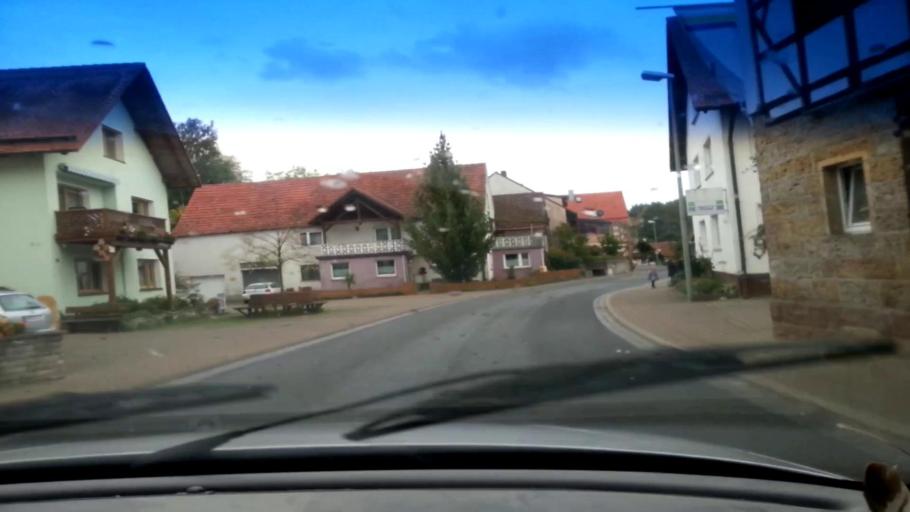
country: DE
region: Bavaria
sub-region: Regierungsbezirk Unterfranken
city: Stettfeld
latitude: 50.0005
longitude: 10.7457
